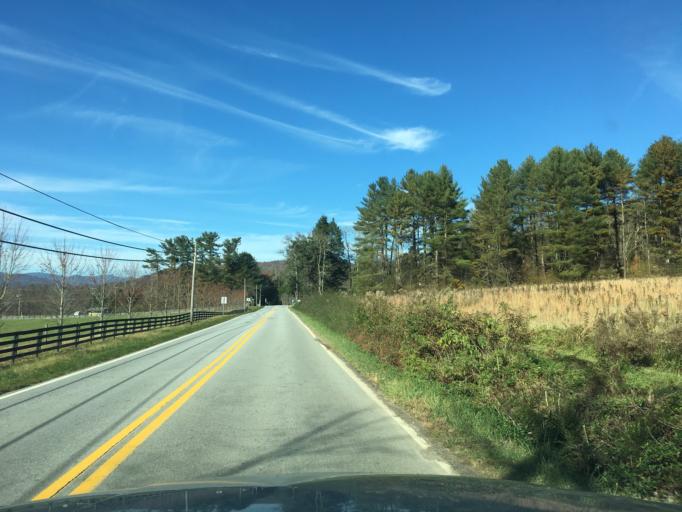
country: US
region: North Carolina
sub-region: Henderson County
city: Etowah
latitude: 35.2526
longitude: -82.6332
